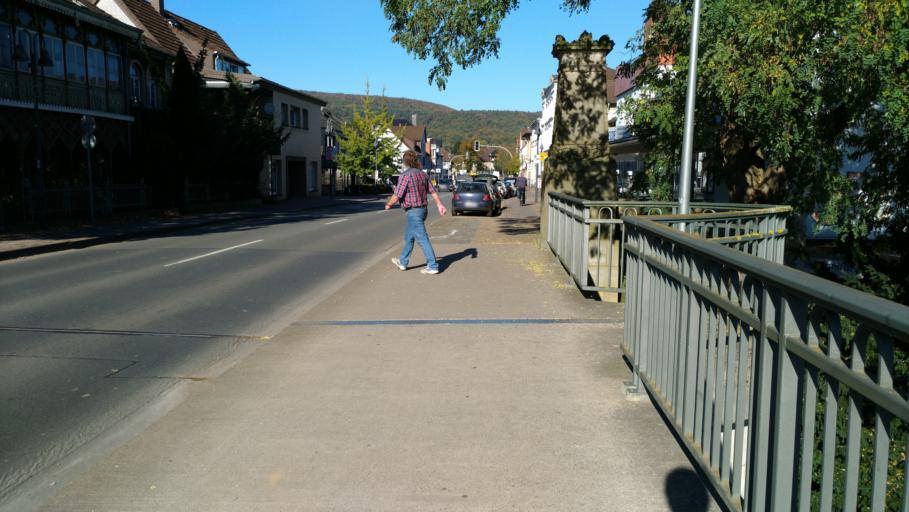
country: DE
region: Lower Saxony
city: Rinteln
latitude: 52.1911
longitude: 9.0816
